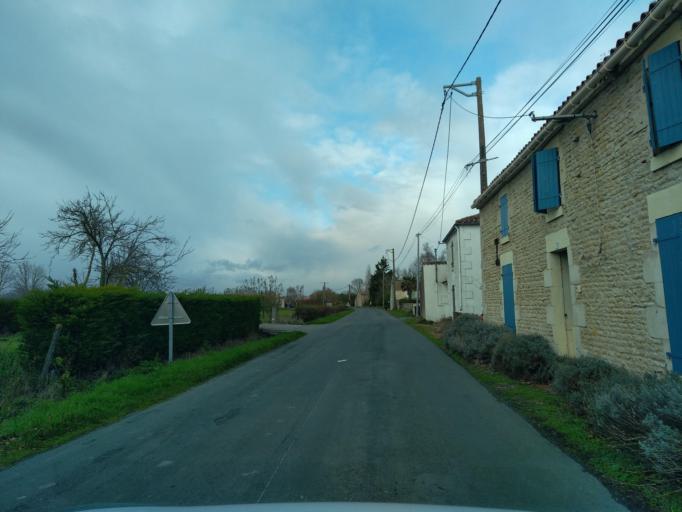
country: FR
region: Pays de la Loire
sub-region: Departement de la Vendee
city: Vix
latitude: 46.3453
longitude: -0.8296
